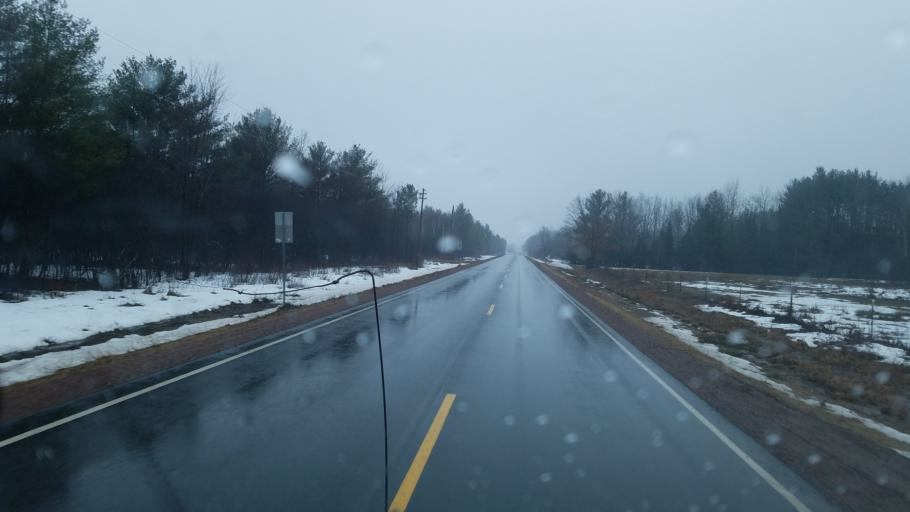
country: US
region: Wisconsin
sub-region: Wood County
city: Marshfield
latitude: 44.5581
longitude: -90.3000
